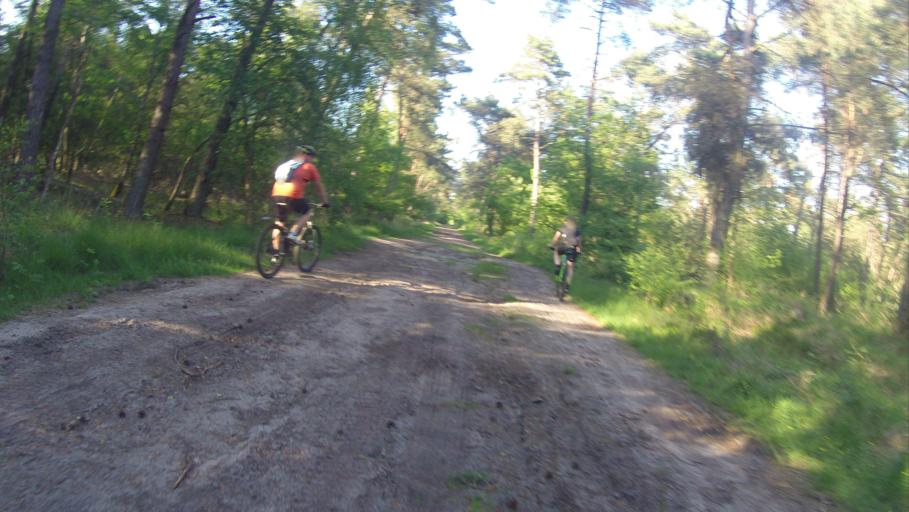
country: NL
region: Gelderland
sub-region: Gemeente Lochem
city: Almen
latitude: 52.1333
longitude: 6.3476
